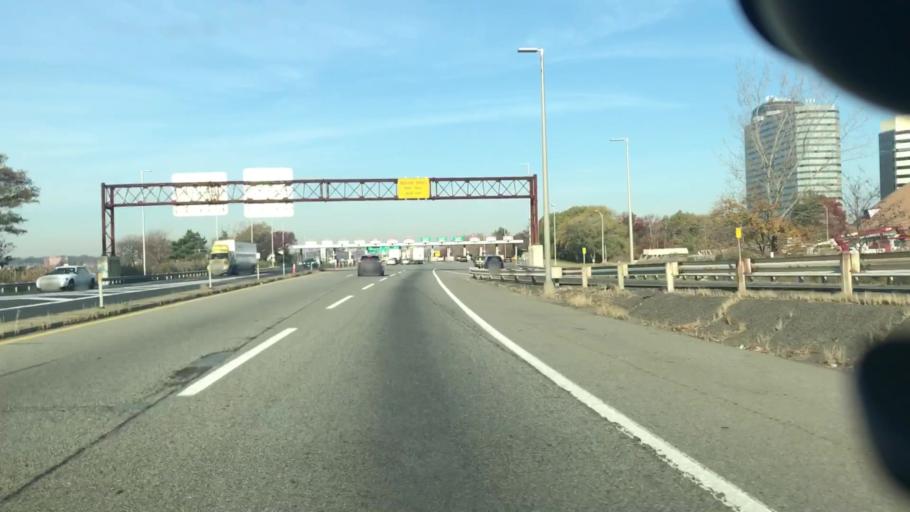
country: US
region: New Jersey
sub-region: Hudson County
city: Secaucus
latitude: 40.8020
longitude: -74.0760
